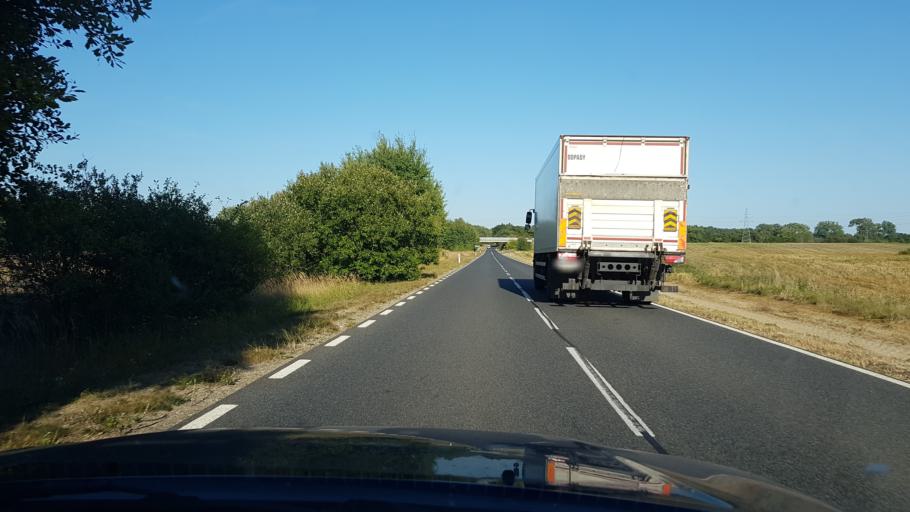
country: PL
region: West Pomeranian Voivodeship
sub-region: Powiat stargardzki
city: Stara Dabrowa
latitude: 53.4338
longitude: 15.1836
